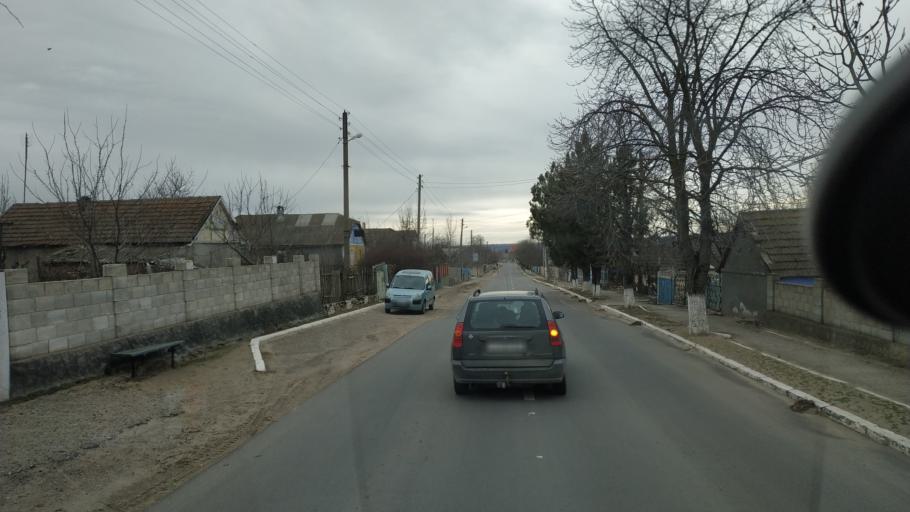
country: MD
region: Telenesti
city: Cocieri
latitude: 47.3019
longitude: 29.1137
